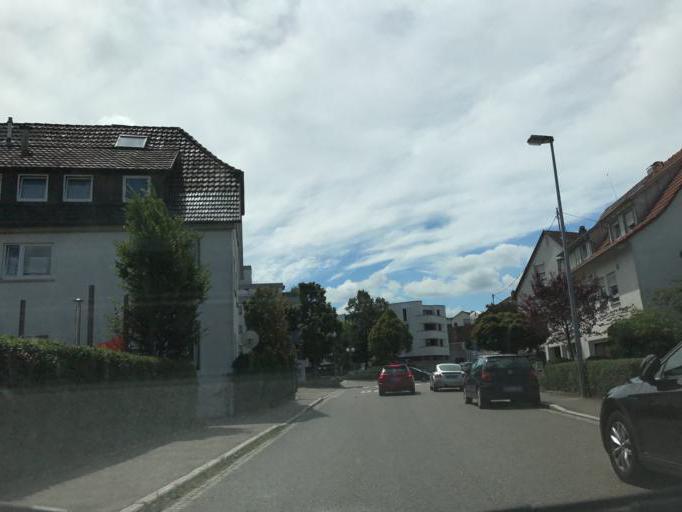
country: DE
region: Baden-Wuerttemberg
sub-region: Regierungsbezirk Stuttgart
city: Waiblingen
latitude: 48.8059
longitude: 9.3228
